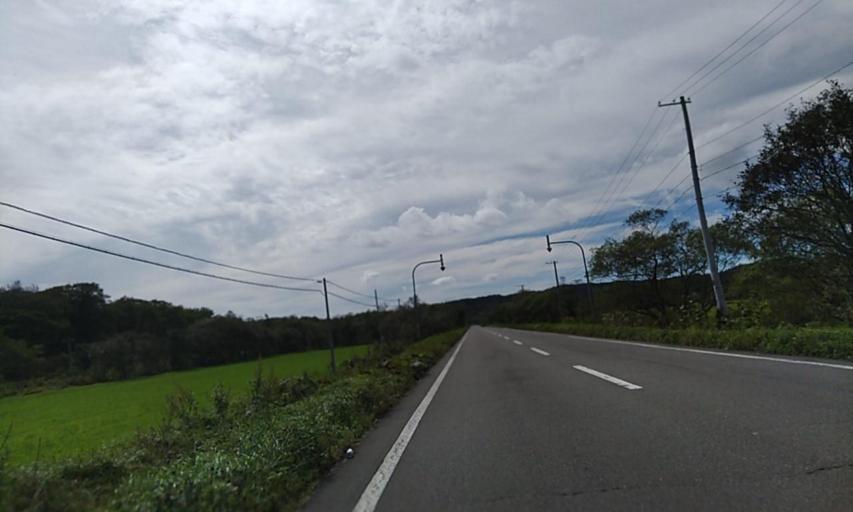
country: JP
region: Hokkaido
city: Kushiro
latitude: 42.8484
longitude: 143.8506
